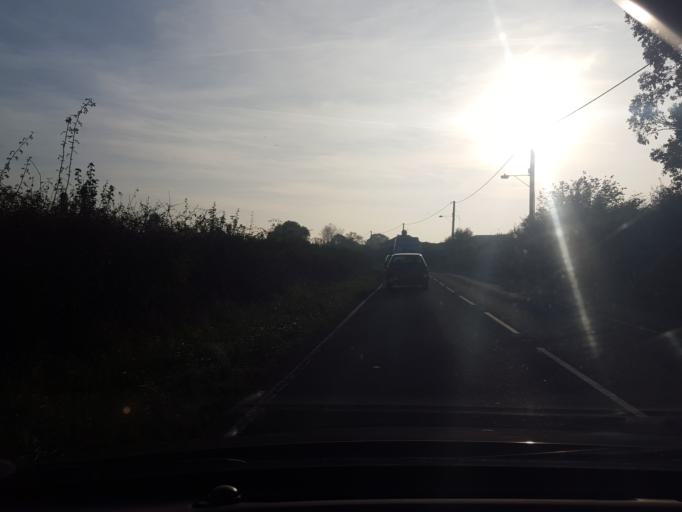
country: GB
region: England
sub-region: Essex
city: Frinton-on-Sea
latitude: 51.8346
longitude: 1.2116
